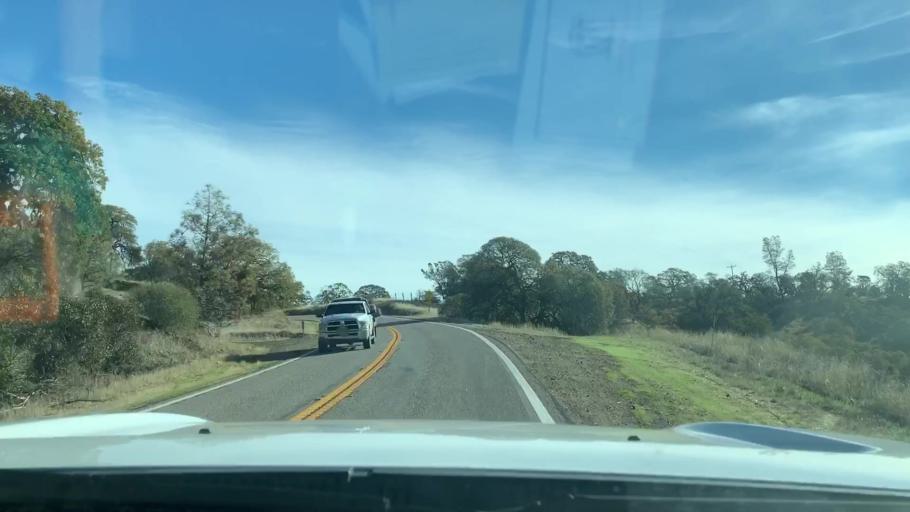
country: US
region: California
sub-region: Monterey County
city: King City
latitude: 36.1926
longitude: -120.7629
